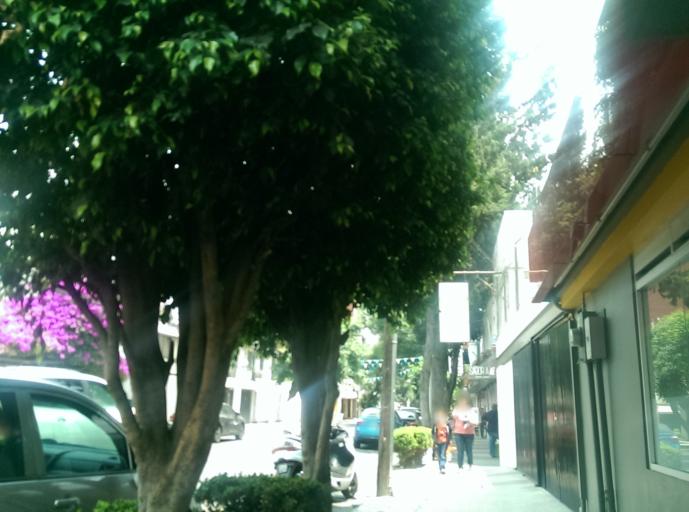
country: MX
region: Mexico City
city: Colonia del Valle
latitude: 19.3752
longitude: -99.1828
